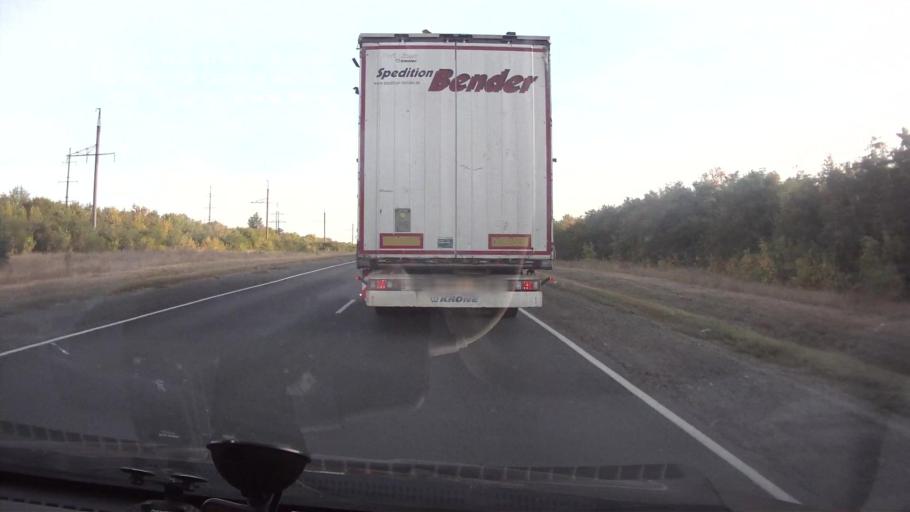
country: RU
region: Saratov
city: Krasnoarmeysk
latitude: 51.1532
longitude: 45.6494
